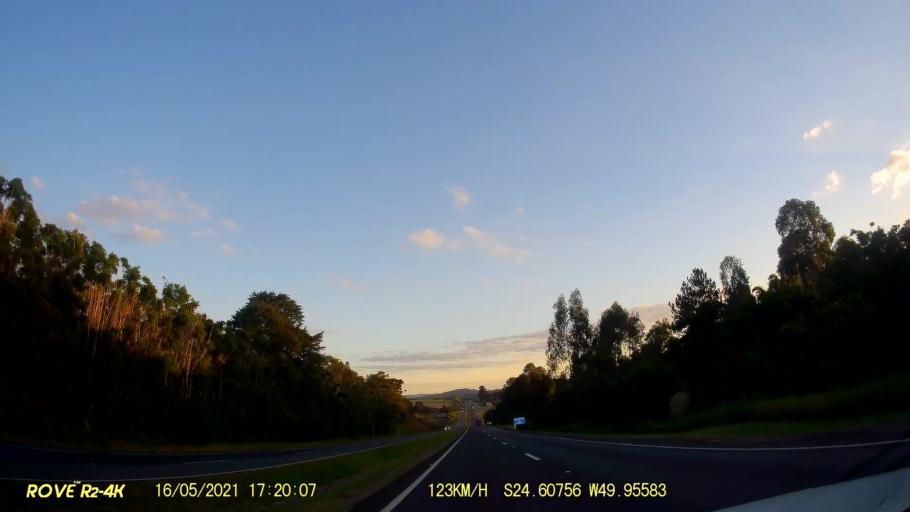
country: BR
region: Parana
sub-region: Pirai Do Sul
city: Pirai do Sul
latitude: -24.6078
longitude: -49.9558
